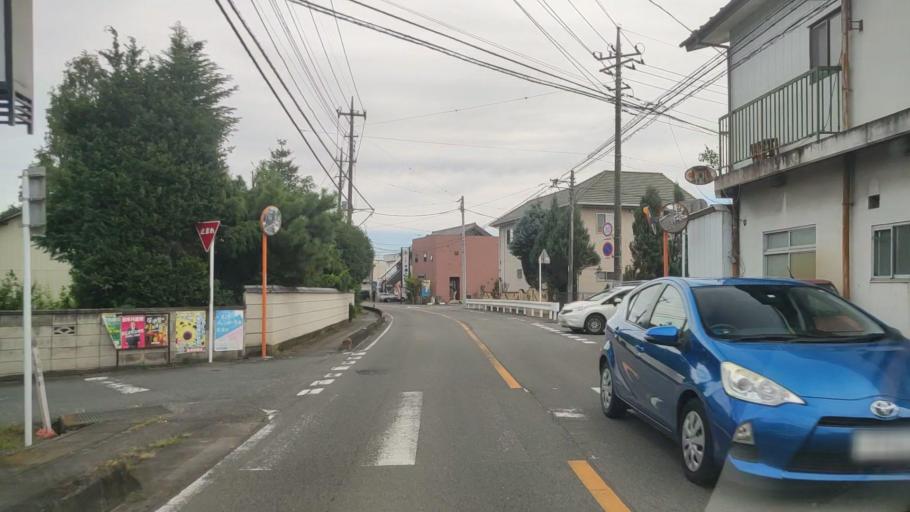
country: JP
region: Gunma
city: Takasaki
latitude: 36.3595
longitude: 138.9873
